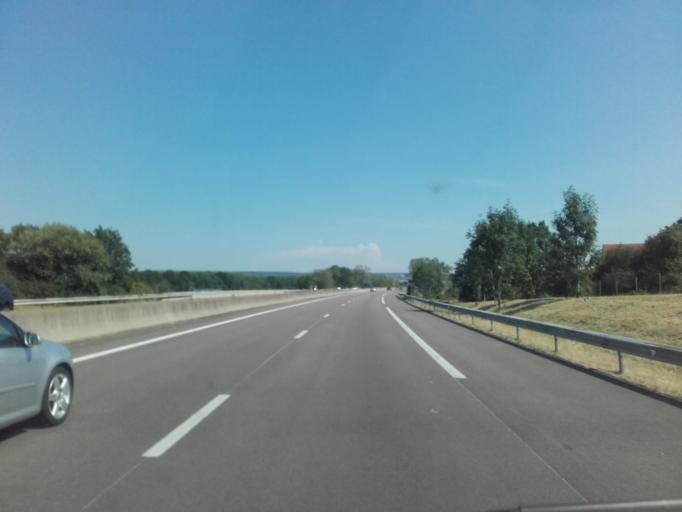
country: FR
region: Bourgogne
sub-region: Departement de la Cote-d'Or
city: Pouilly-en-Auxois
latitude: 47.2495
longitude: 4.5663
